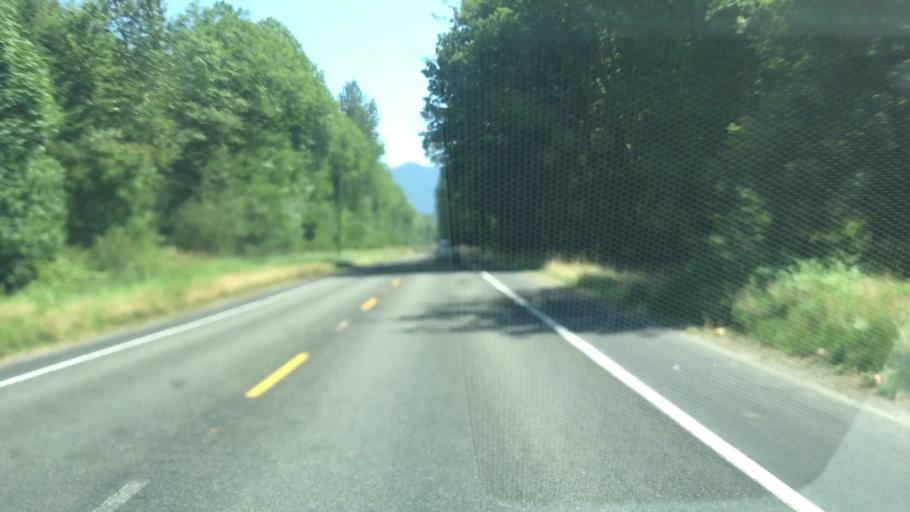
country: US
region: Washington
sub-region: Snohomish County
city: Gold Bar
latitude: 47.7612
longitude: -121.4713
